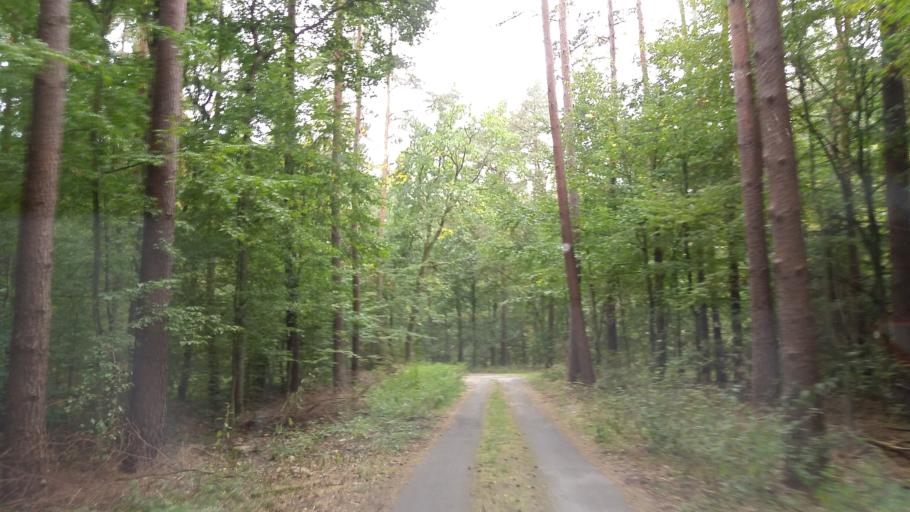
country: PL
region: West Pomeranian Voivodeship
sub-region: Powiat mysliborski
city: Barlinek
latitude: 52.9634
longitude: 15.2923
